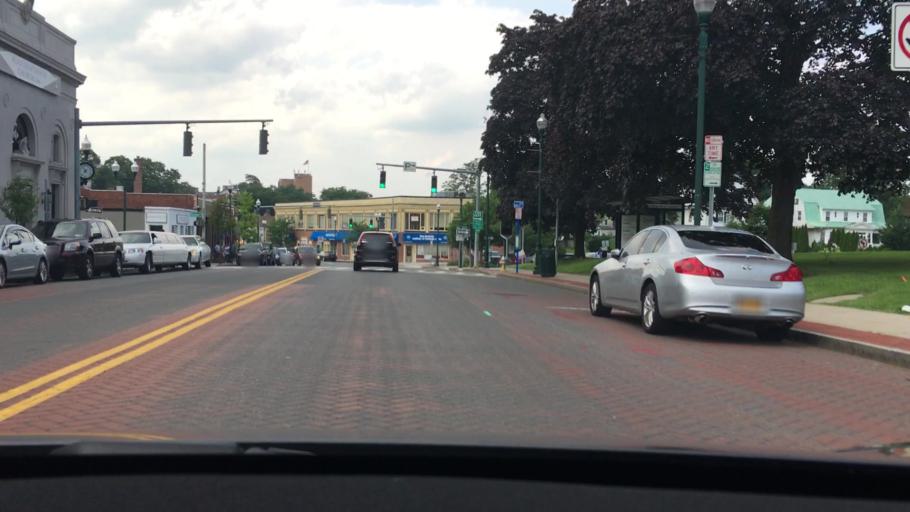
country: US
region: New York
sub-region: Westchester County
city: New Rochelle
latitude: 40.9200
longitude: -73.7869
